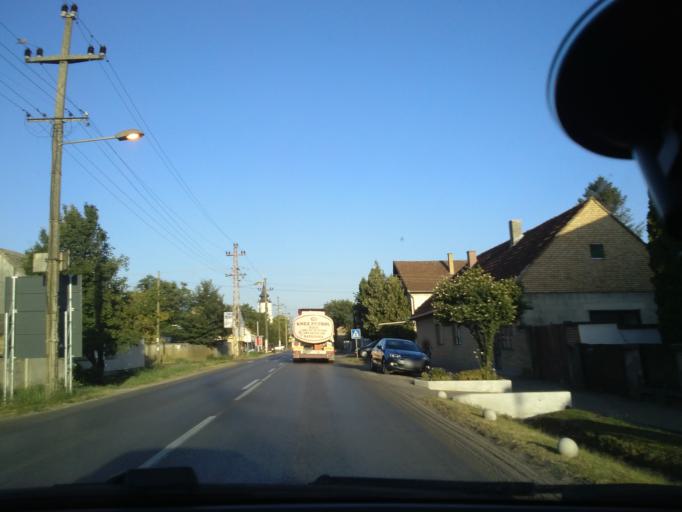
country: RS
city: Rumenka
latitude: 45.2937
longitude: 19.7387
